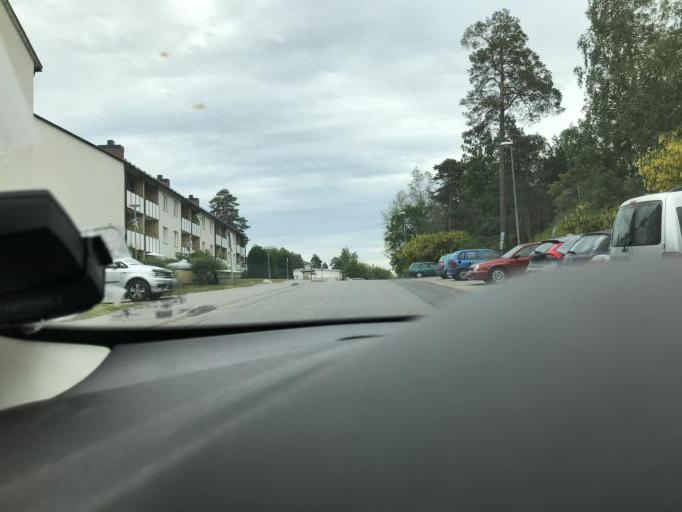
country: SE
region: Stockholm
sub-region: Botkyrka Kommun
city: Tumba
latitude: 59.1943
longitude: 17.8120
